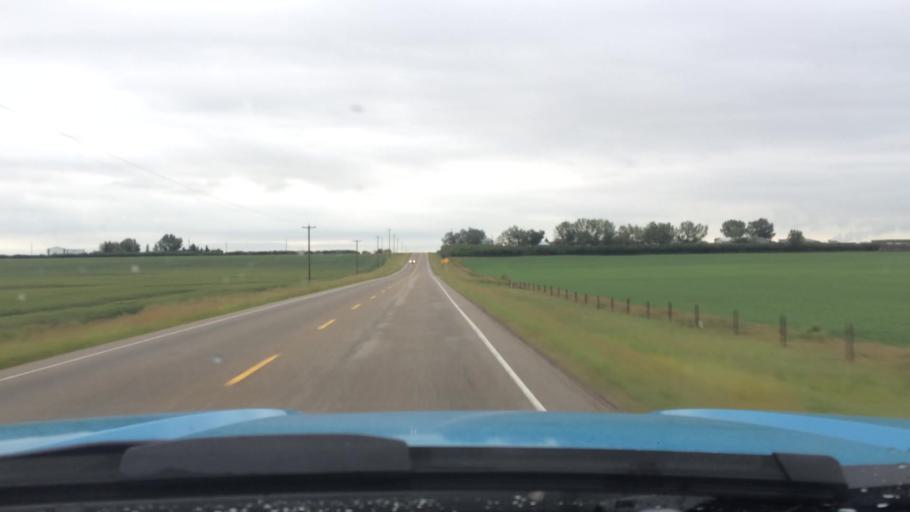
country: CA
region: Alberta
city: Airdrie
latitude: 51.2125
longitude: -114.0441
